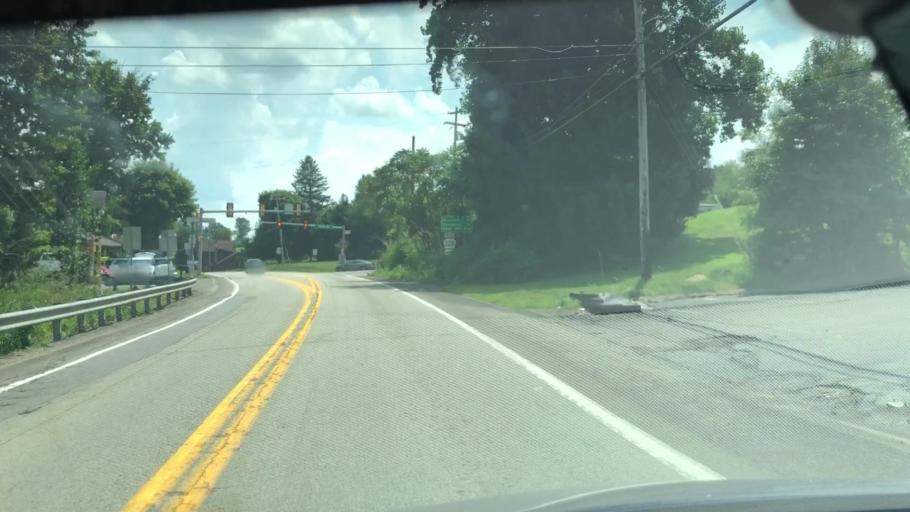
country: US
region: Pennsylvania
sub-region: Butler County
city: Saxonburg
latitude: 40.7202
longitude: -79.7560
